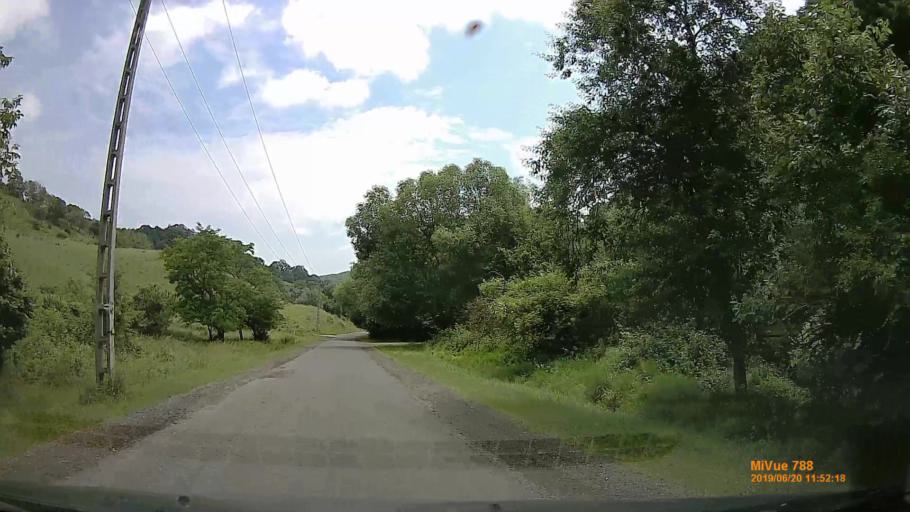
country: HU
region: Baranya
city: Mecseknadasd
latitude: 46.2205
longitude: 18.4175
